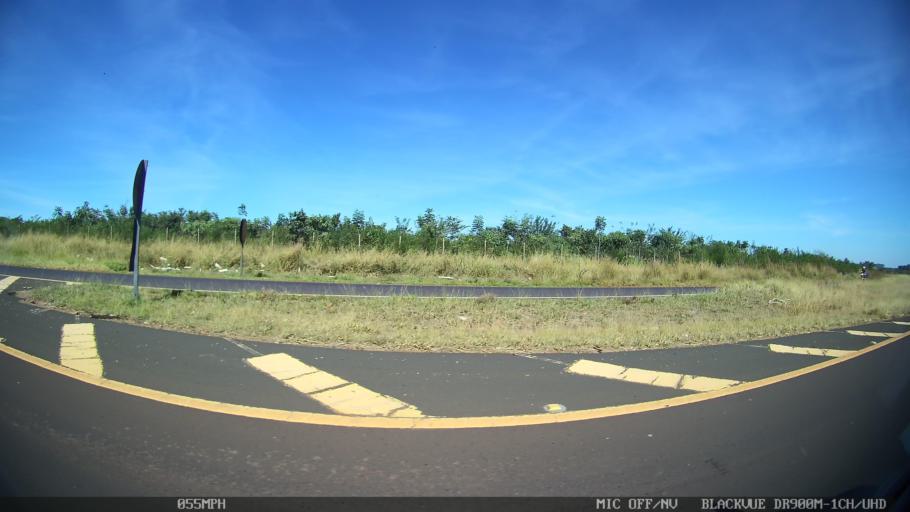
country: BR
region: Sao Paulo
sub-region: Franca
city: Franca
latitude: -20.5461
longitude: -47.4761
